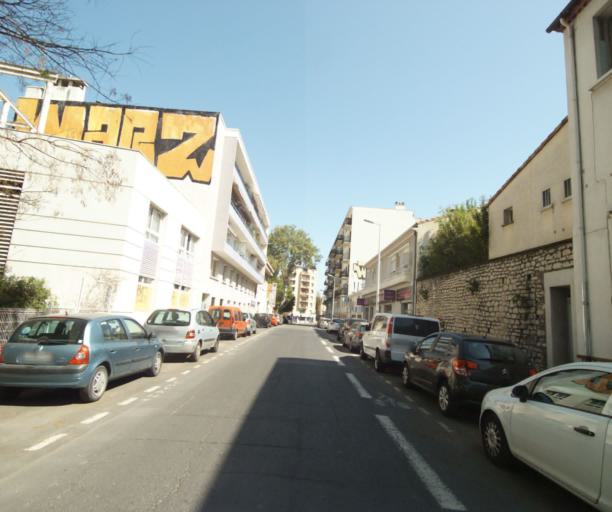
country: FR
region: Languedoc-Roussillon
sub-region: Departement de l'Herault
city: Montpellier
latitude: 43.6014
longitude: 3.8831
